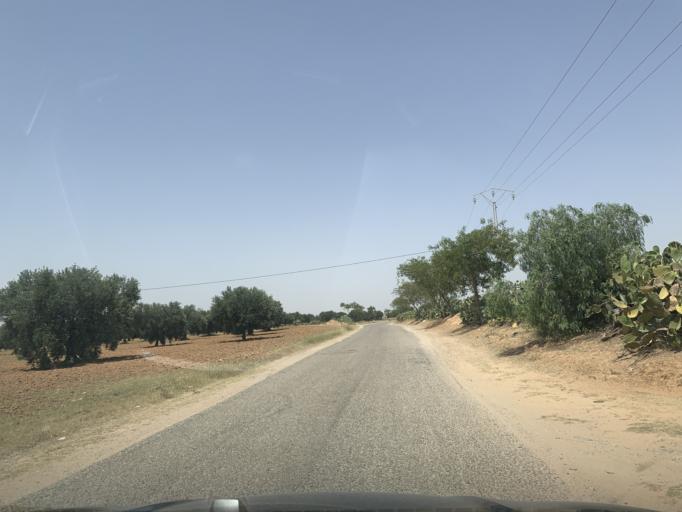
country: TN
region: Al Mahdiyah
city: Shurban
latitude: 35.1860
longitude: 10.2428
